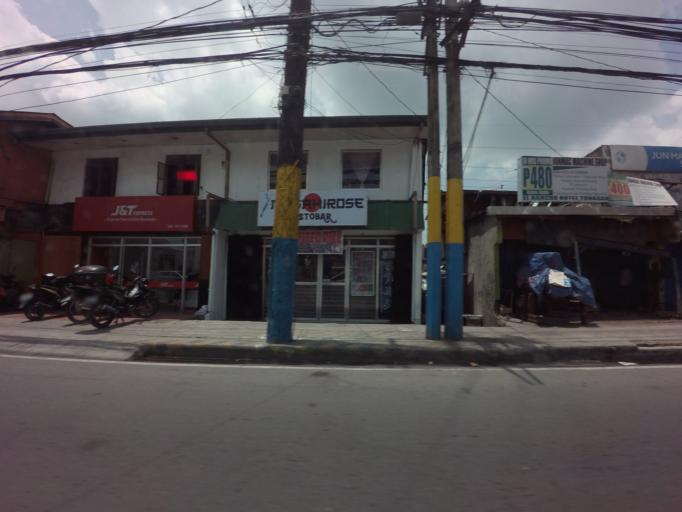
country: PH
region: Calabarzon
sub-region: Province of Laguna
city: San Pedro
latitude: 14.4044
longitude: 121.0470
